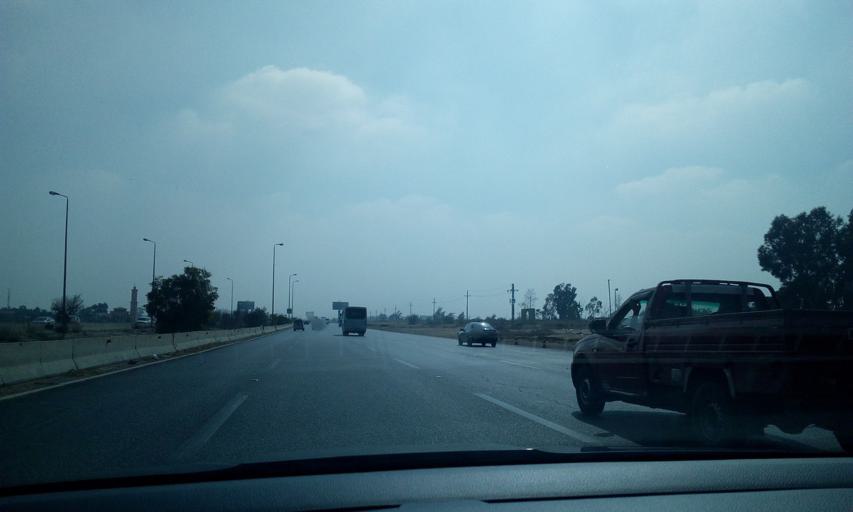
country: EG
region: Eastern Province
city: Bilbays
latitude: 30.1871
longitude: 31.6329
